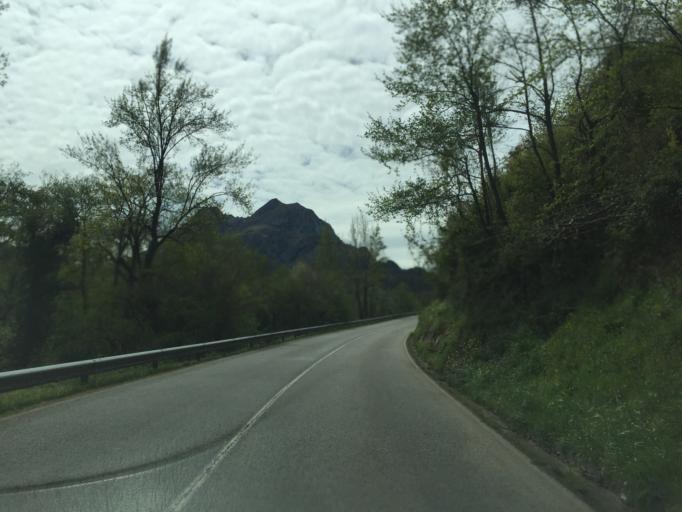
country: ES
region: Asturias
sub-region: Province of Asturias
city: Proaza
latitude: 43.2611
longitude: -6.0075
